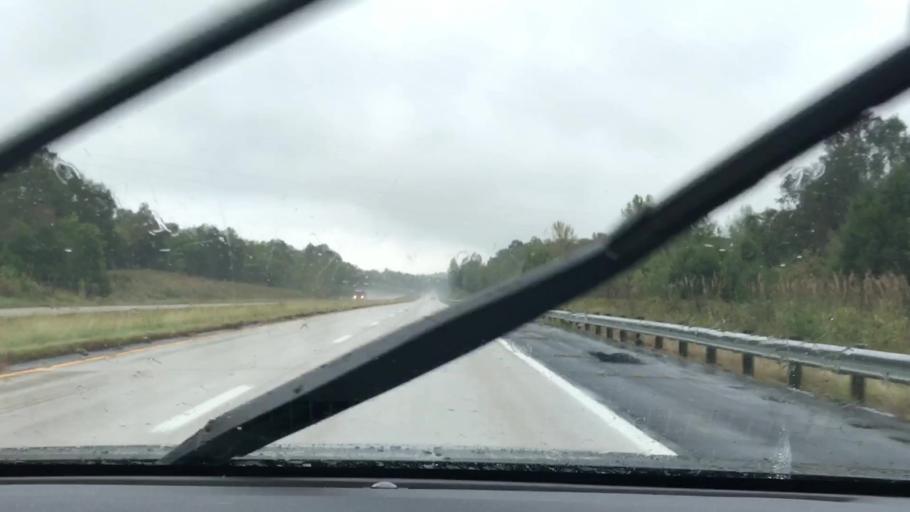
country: US
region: Kentucky
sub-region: Hopkins County
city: Nortonville
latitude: 37.1397
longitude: -87.4618
